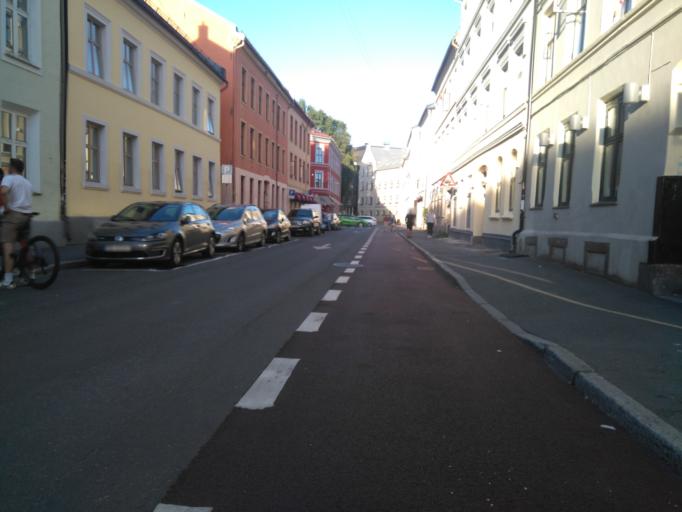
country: NO
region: Oslo
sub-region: Oslo
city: Oslo
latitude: 59.9201
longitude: 10.7581
